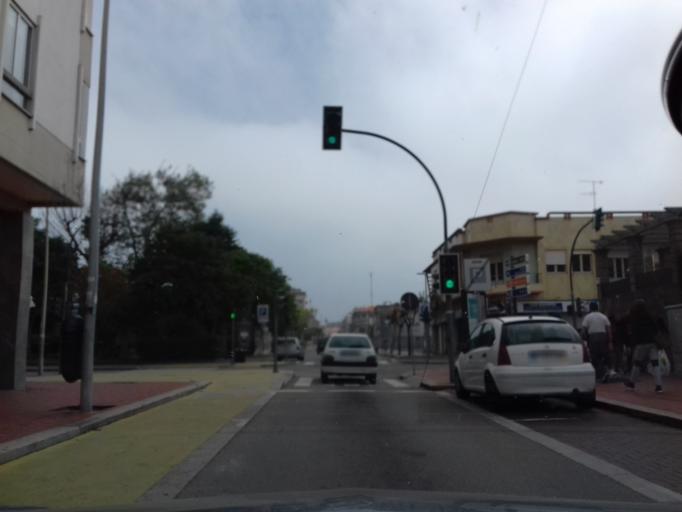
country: PT
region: Aveiro
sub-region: Espinho
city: Espinho
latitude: 41.0072
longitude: -8.6402
